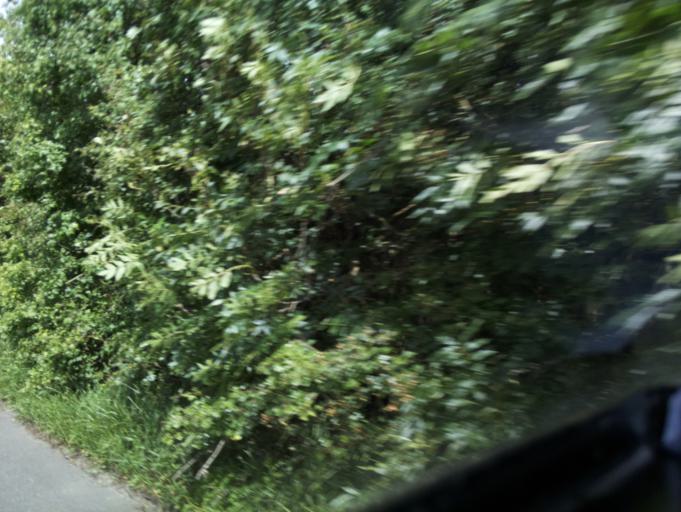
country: GB
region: England
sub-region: Nottinghamshire
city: Cotgrave
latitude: 52.8968
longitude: -1.0801
